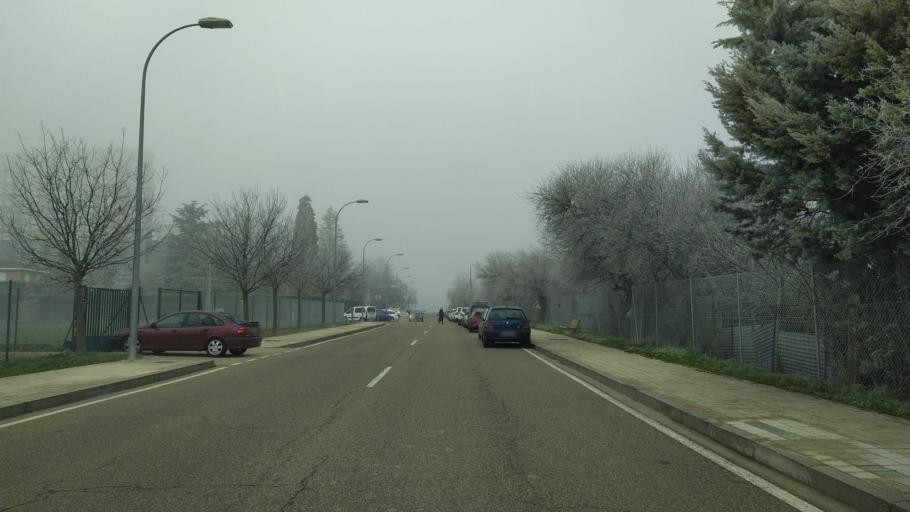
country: ES
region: Castille and Leon
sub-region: Provincia de Palencia
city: Palencia
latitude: 41.9992
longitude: -4.5381
